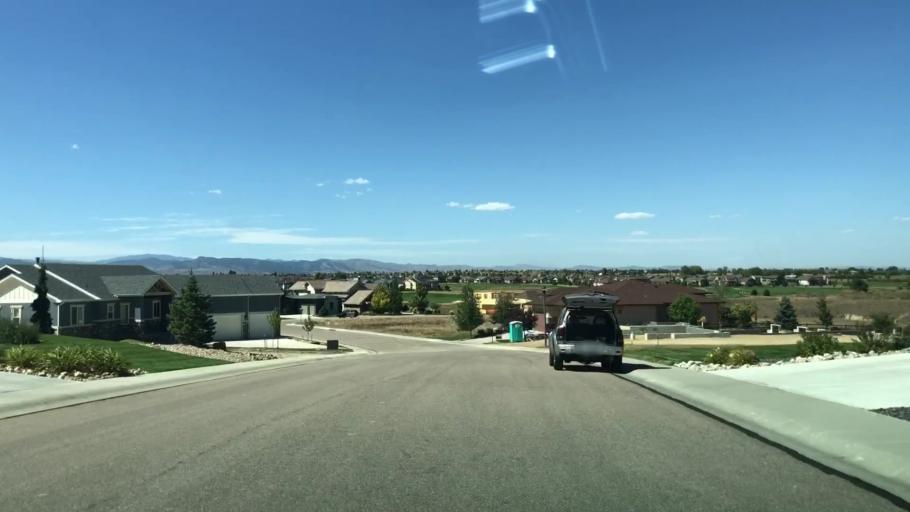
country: US
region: Colorado
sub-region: Weld County
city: Windsor
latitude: 40.4539
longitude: -104.9601
